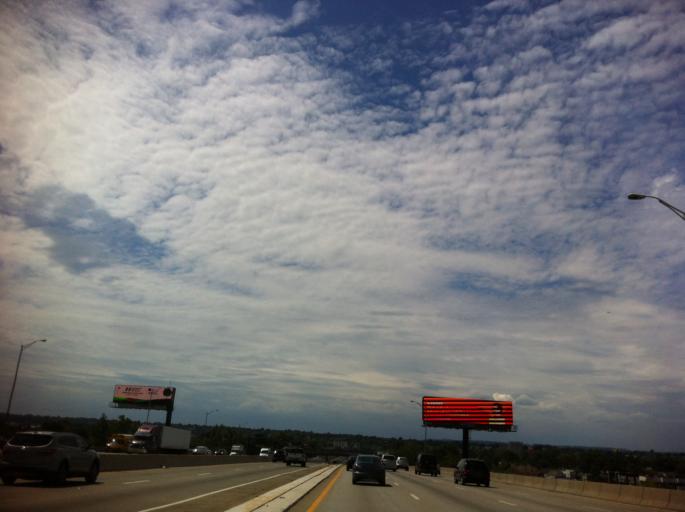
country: US
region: New Jersey
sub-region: Bergen County
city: Ridgefield Park
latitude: 40.8665
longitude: -74.0240
